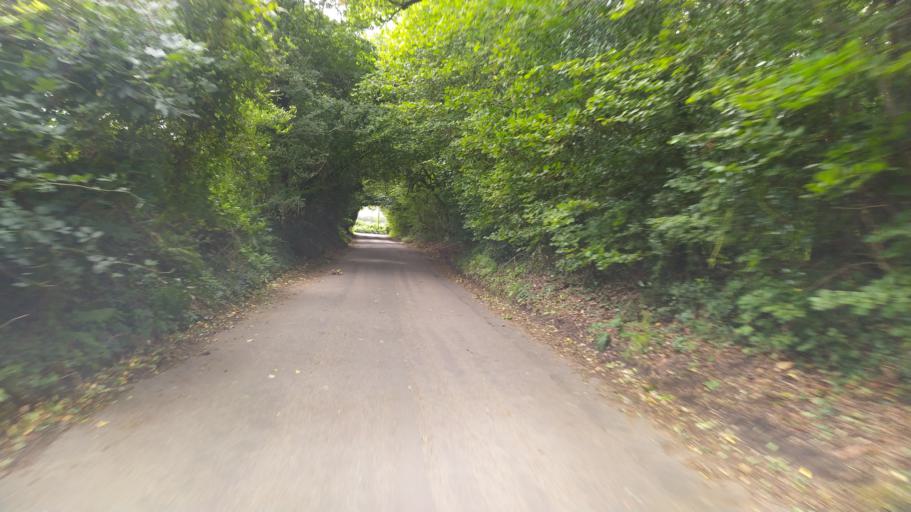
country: GB
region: England
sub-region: Dorset
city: Broadstone
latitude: 50.7729
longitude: -2.0346
